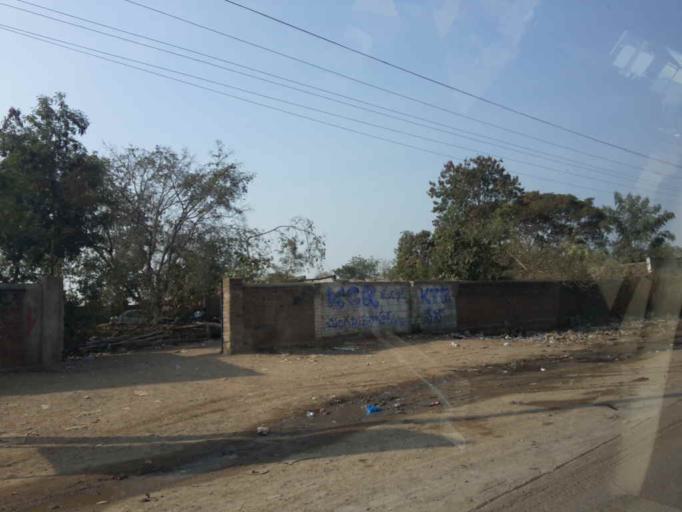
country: IN
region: Telangana
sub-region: Karimnagar
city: Kottapalli
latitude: 18.4317
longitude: 79.0154
